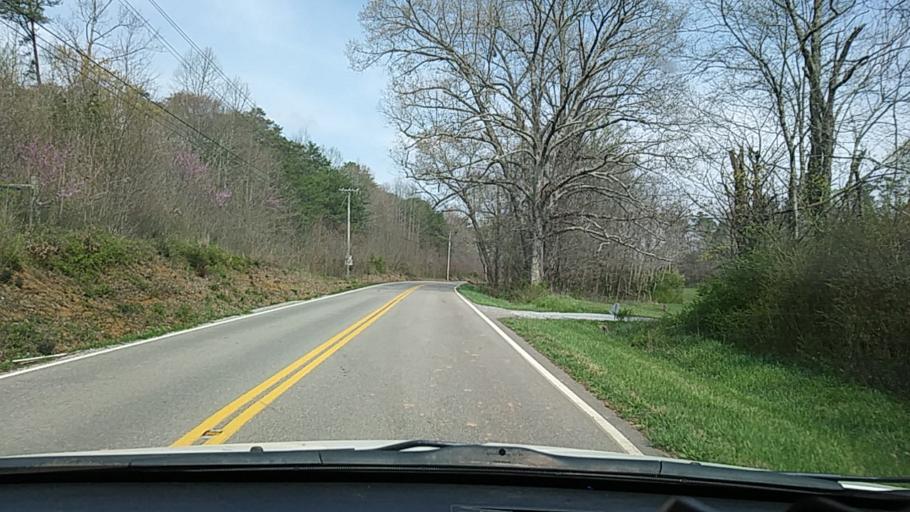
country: US
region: Tennessee
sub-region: Greene County
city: Greeneville
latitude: 36.0950
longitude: -82.7913
